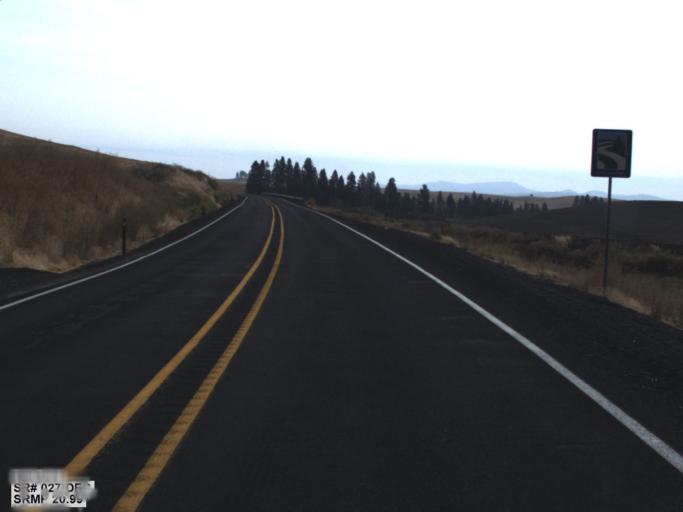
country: US
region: Washington
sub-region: Whitman County
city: Pullman
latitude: 46.9691
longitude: -117.1178
